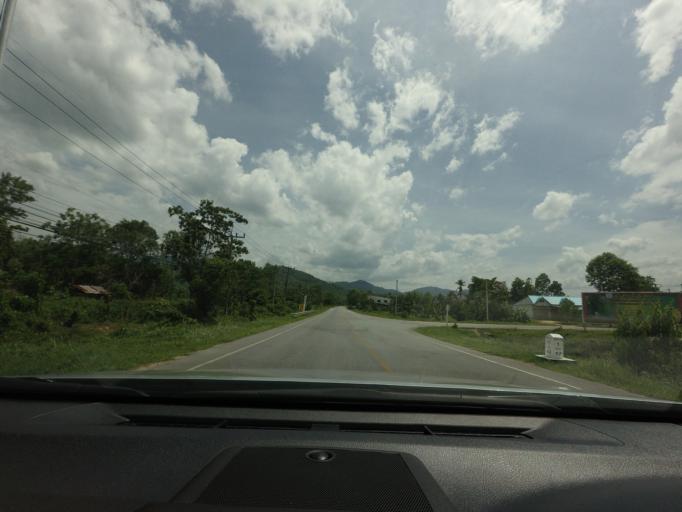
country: TH
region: Yala
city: Raman
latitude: 6.4555
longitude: 101.3565
